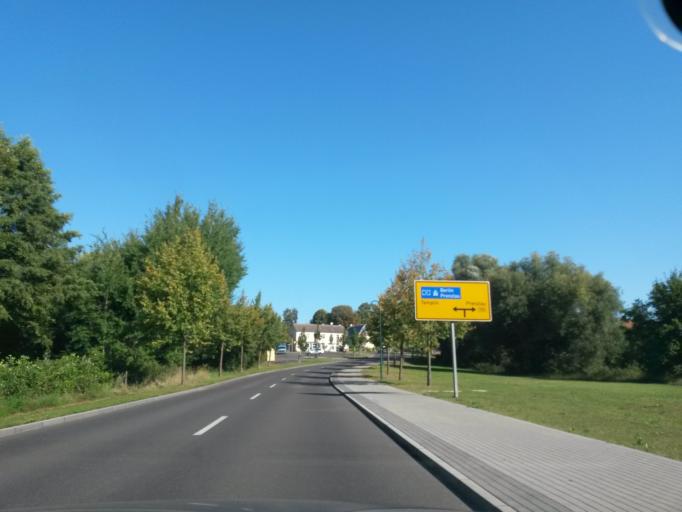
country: DE
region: Brandenburg
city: Angermunde
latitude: 53.0858
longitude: 13.9557
